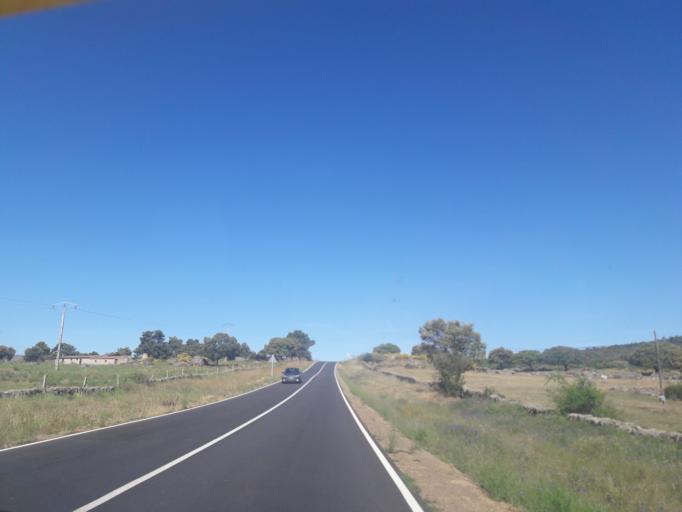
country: ES
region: Castille and Leon
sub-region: Provincia de Salamanca
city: Santibanez de Bejar
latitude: 40.4809
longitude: -5.6398
